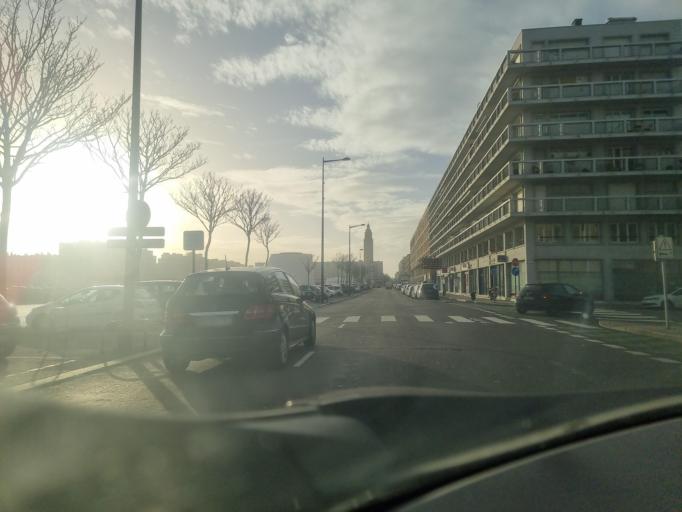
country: FR
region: Haute-Normandie
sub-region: Departement de la Seine-Maritime
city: Le Havre
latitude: 49.4909
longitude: 0.1117
